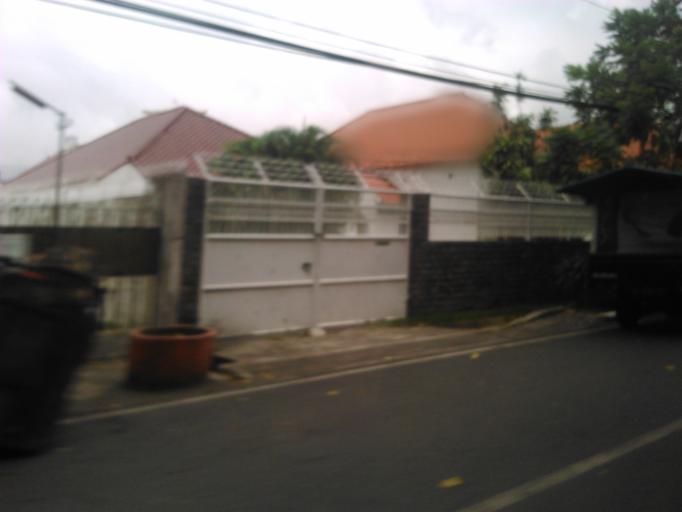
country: ID
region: East Java
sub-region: Kota Surabaya
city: Surabaya
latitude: -7.2608
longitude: 112.7269
